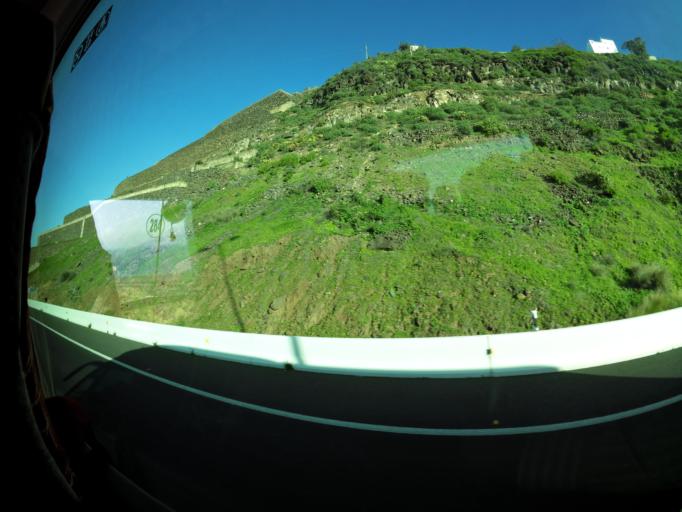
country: ES
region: Canary Islands
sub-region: Provincia de Las Palmas
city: Moya
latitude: 28.1401
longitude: -15.5871
